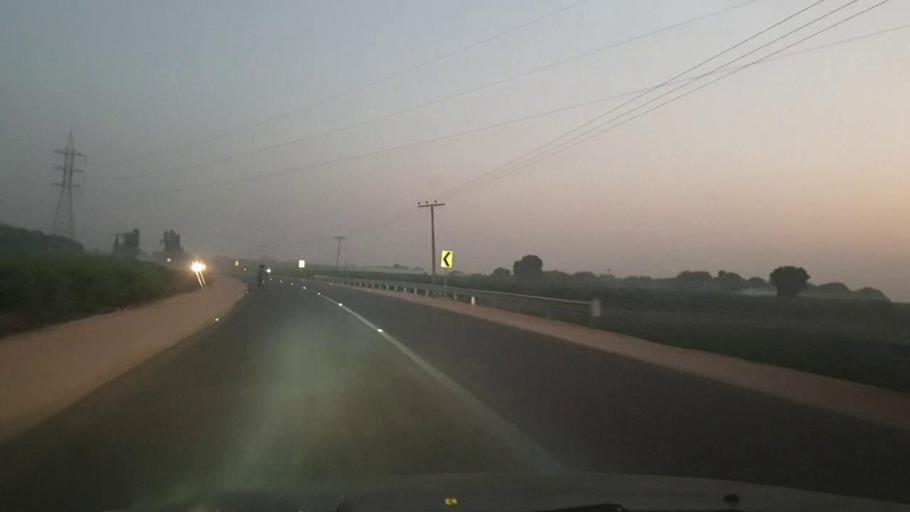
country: PK
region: Sindh
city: Tando Allahyar
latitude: 25.4125
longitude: 68.7556
